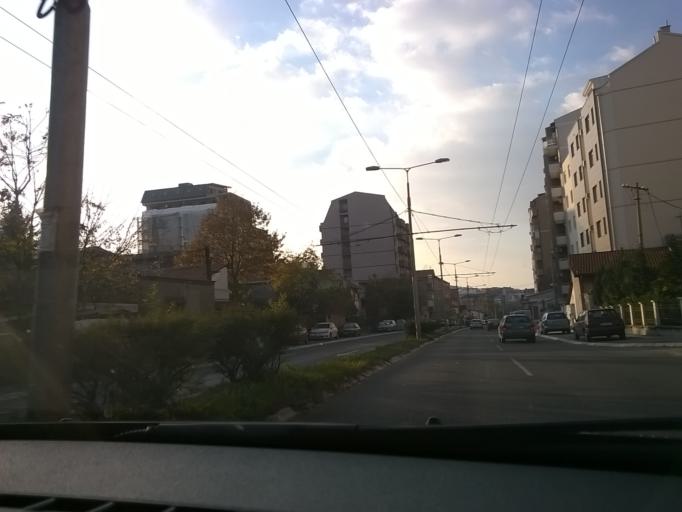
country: RS
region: Central Serbia
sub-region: Belgrade
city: Vracar
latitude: 44.8008
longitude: 20.4953
